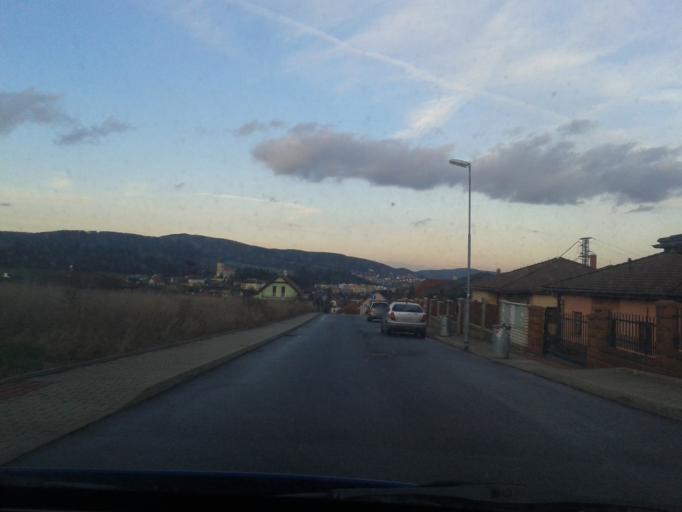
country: CZ
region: Central Bohemia
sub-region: Okres Beroun
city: Kraluv Dvur
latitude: 49.9349
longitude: 14.0151
